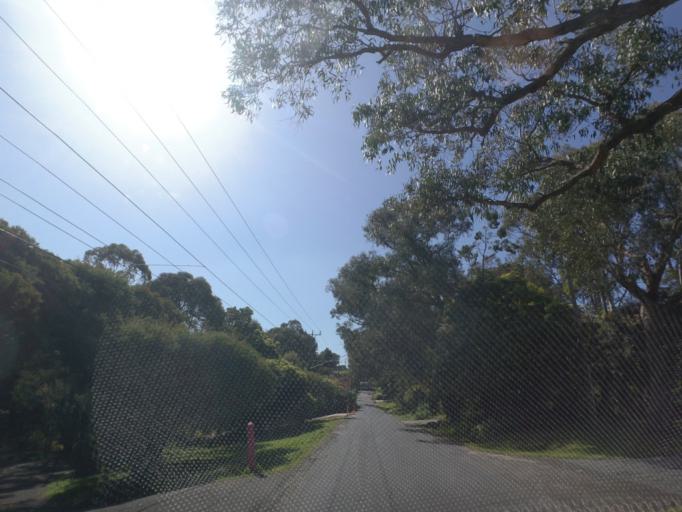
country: AU
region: Victoria
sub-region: Manningham
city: Park Orchards
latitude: -37.7883
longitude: 145.2264
